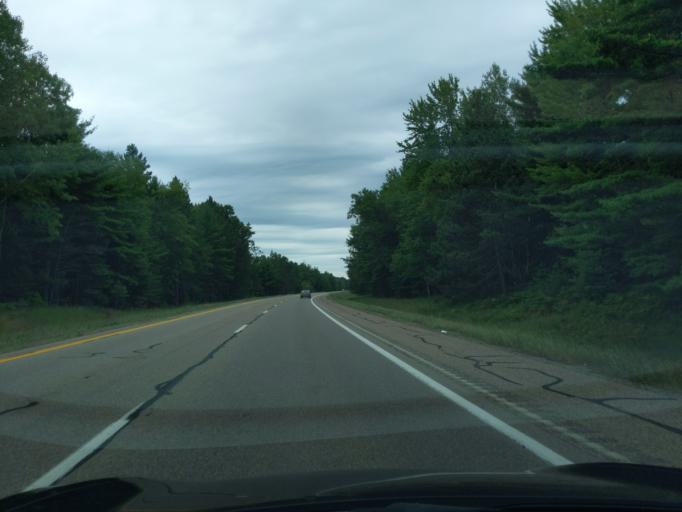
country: US
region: Michigan
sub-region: Roscommon County
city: Houghton Lake
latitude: 44.2245
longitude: -84.7972
